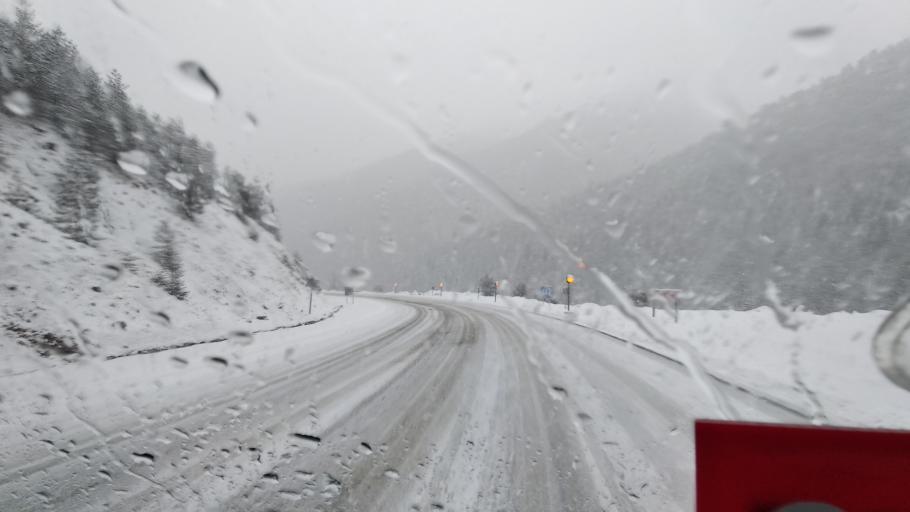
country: TR
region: Gumushane
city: Yaglidere
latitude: 40.6579
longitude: 39.4118
